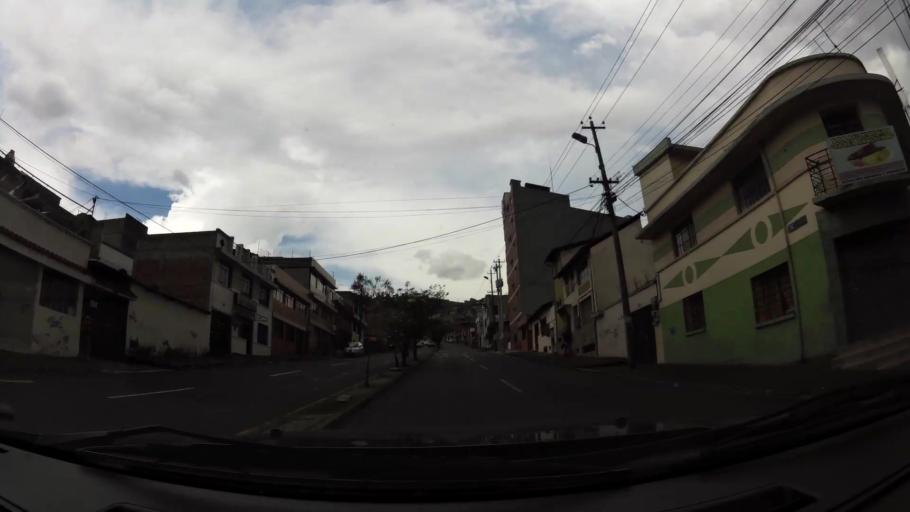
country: EC
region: Pichincha
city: Quito
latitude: -0.2451
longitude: -78.5105
